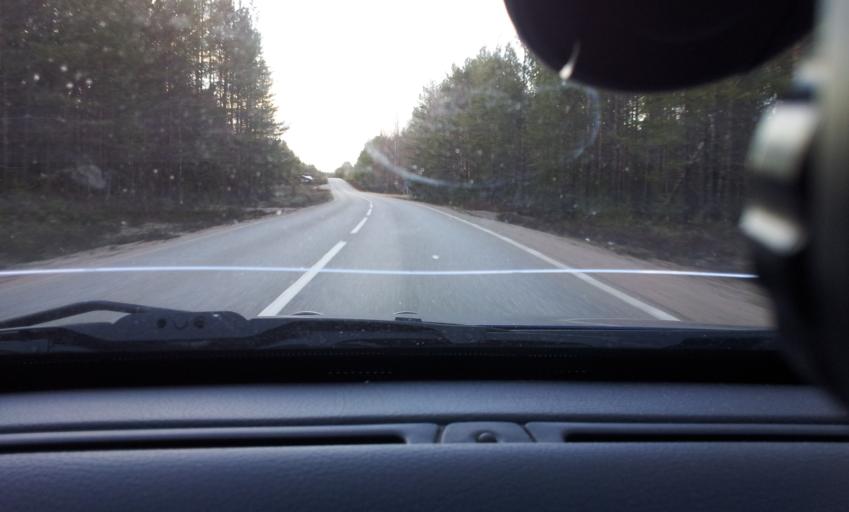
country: SE
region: Vaesternorrland
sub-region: Ange Kommun
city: Ange
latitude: 62.0910
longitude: 15.0910
